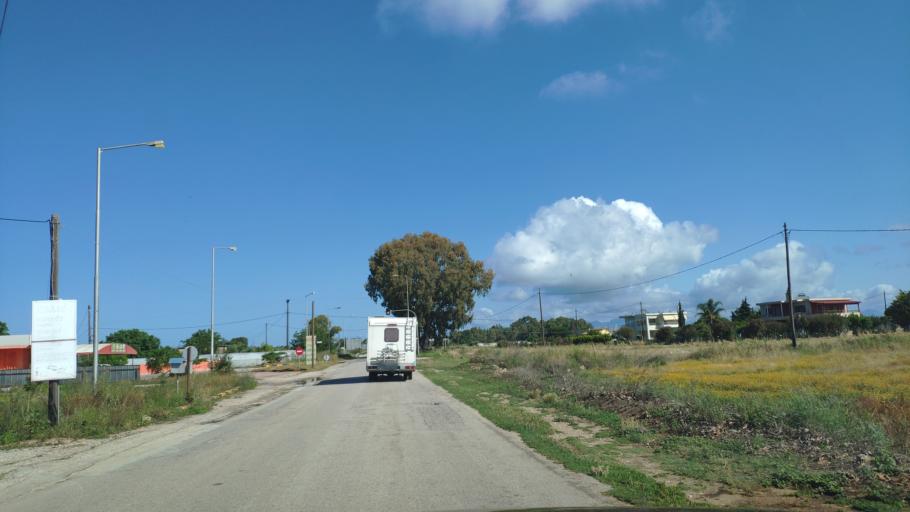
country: GR
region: Epirus
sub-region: Nomos Prevezis
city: Preveza
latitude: 38.9353
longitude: 20.7701
